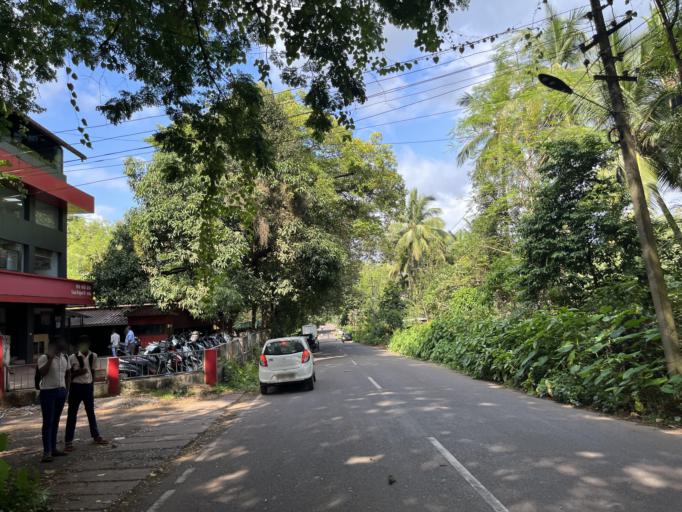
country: IN
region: Goa
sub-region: North Goa
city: Ponda
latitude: 15.4045
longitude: 74.0161
